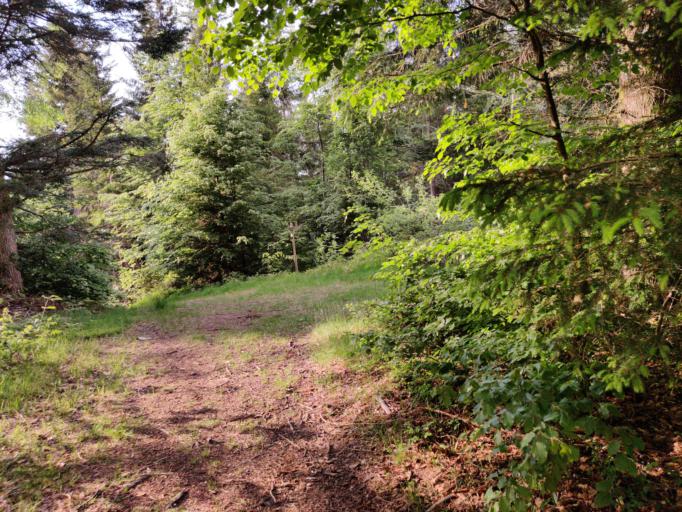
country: DE
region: Baden-Wuerttemberg
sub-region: Freiburg Region
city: Hinterzarten
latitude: 47.8862
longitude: 8.1103
